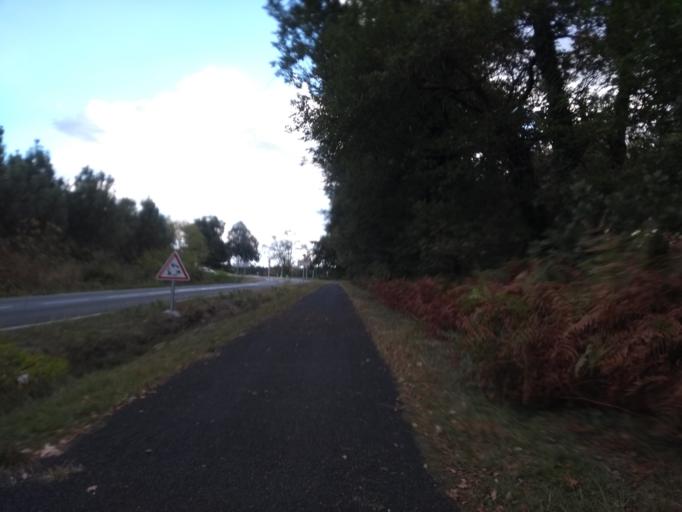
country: FR
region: Aquitaine
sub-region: Departement de la Gironde
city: Cestas
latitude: 44.7171
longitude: -0.6916
